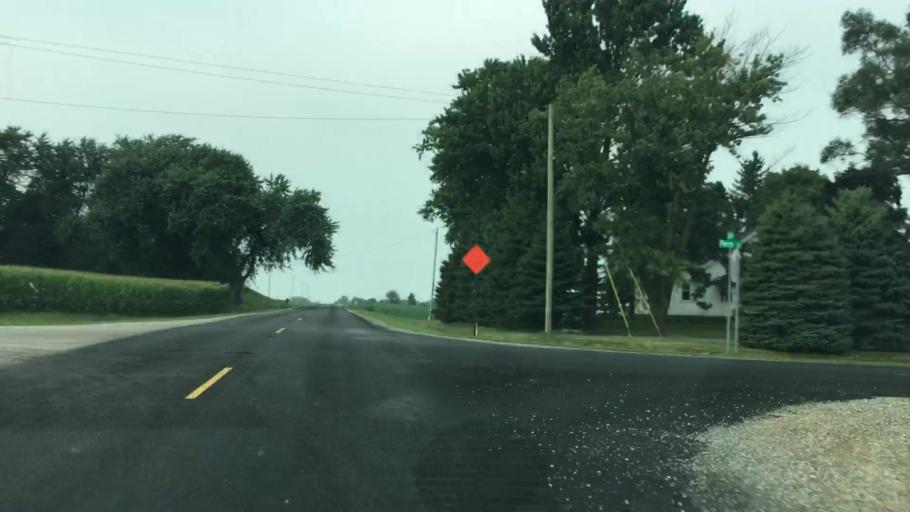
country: US
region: Michigan
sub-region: Ottawa County
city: Hudsonville
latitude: 42.7967
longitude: -85.9008
